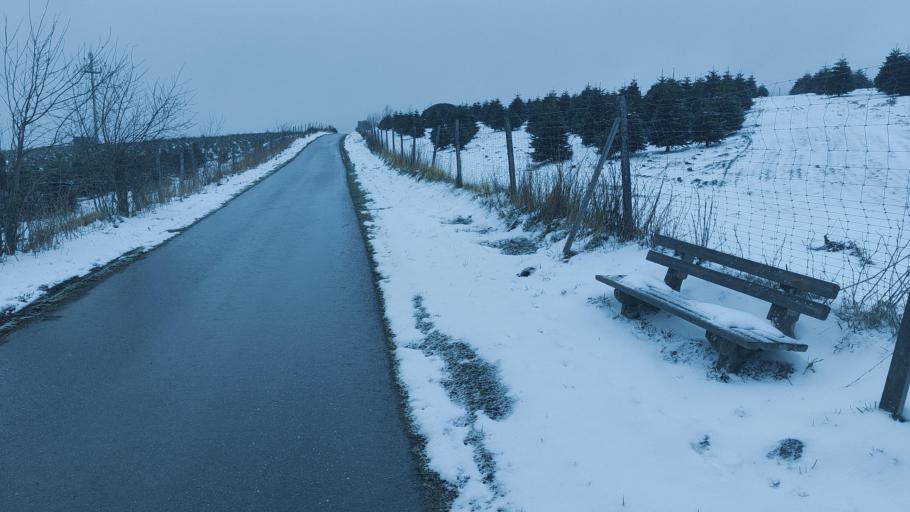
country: DE
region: North Rhine-Westphalia
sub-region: Regierungsbezirk Arnsberg
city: Bad Berleburg
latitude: 51.1485
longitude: 8.4214
